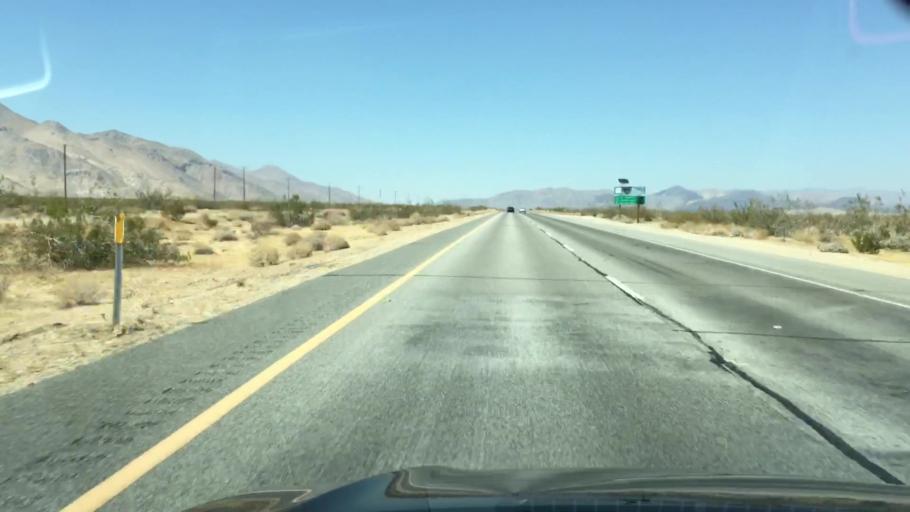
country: US
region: California
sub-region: Kern County
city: Inyokern
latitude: 35.7267
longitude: -117.8689
